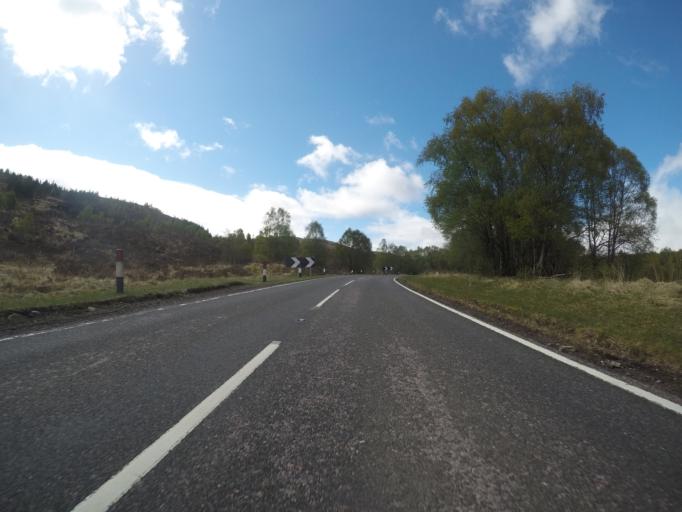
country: GB
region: Scotland
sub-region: Highland
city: Spean Bridge
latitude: 57.1265
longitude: -4.9653
